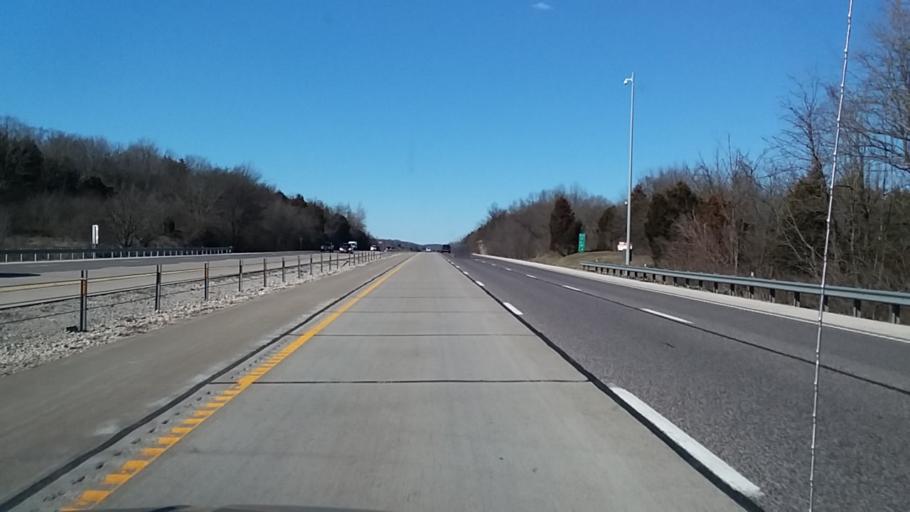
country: US
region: Missouri
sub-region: Jefferson County
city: Pevely
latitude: 38.3087
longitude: -90.4023
